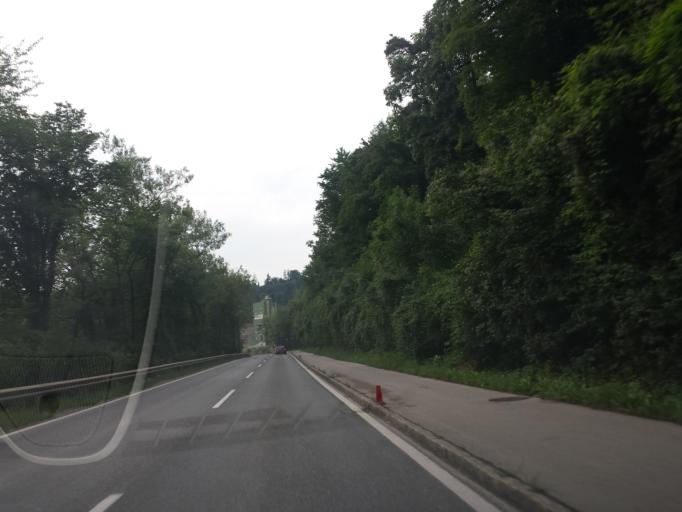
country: AT
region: Styria
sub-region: Graz Stadt
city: Goesting
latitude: 47.1174
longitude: 15.3752
